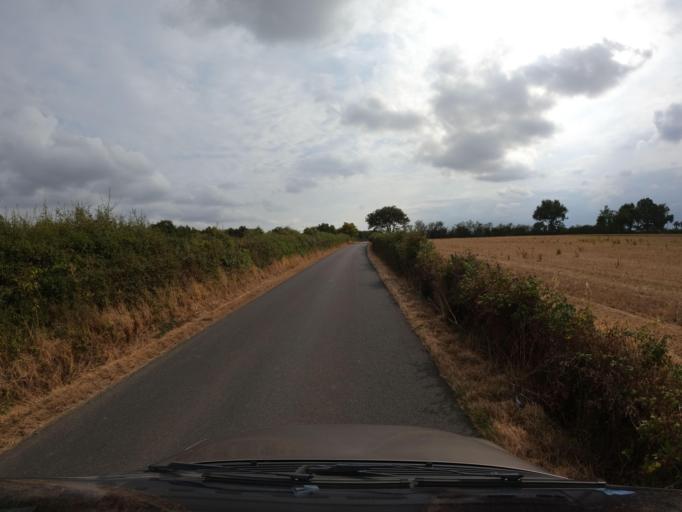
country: FR
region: Pays de la Loire
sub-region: Departement de Maine-et-Loire
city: La Seguiniere
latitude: 47.0448
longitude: -0.9256
